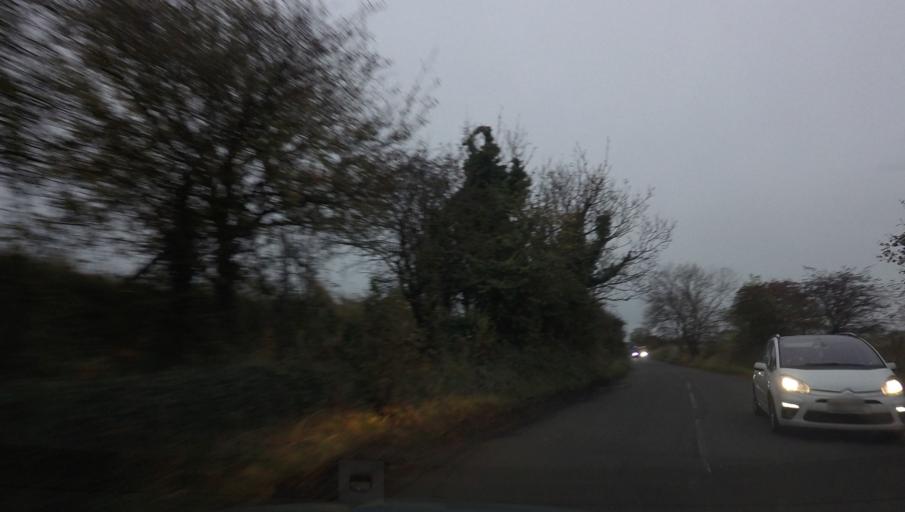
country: GB
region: Scotland
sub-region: Fife
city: Crossford
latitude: 56.0429
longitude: -3.5057
